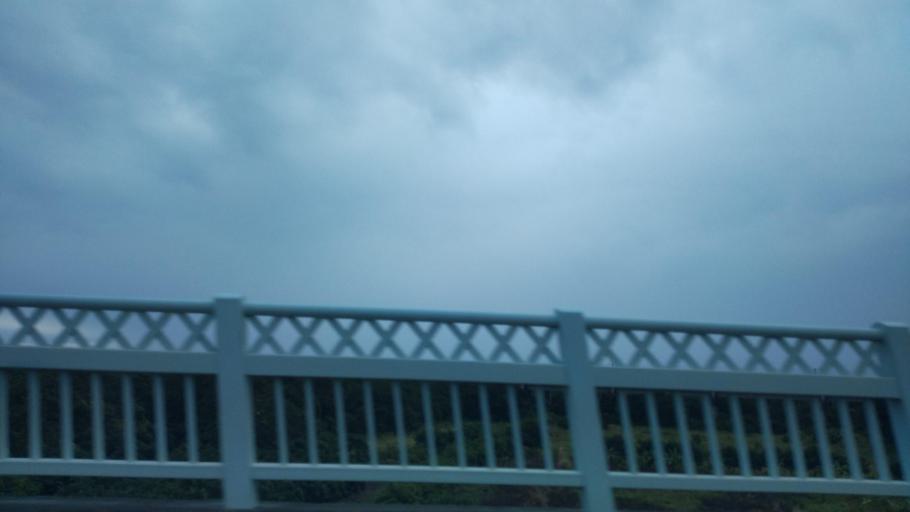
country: TW
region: Taiwan
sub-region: Hualien
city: Hualian
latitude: 24.1390
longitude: 121.6438
